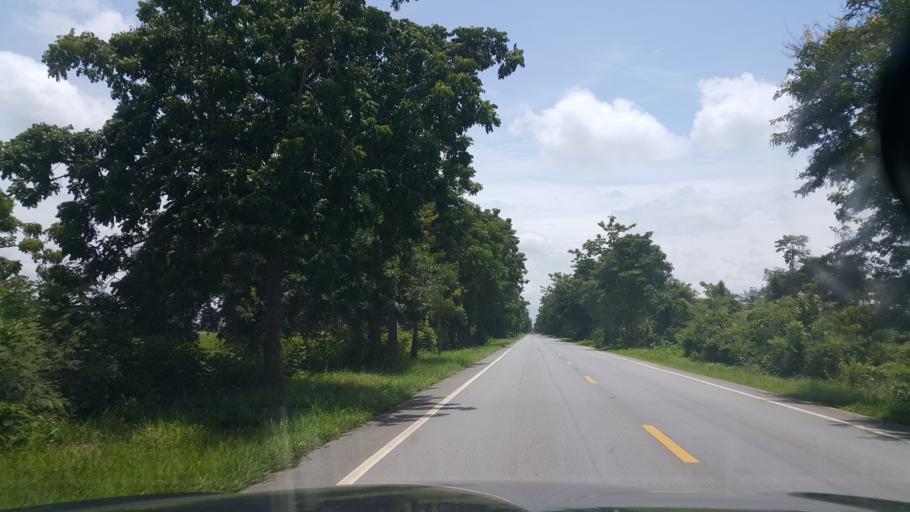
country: TH
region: Sukhothai
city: Sawankhalok
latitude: 17.3269
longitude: 99.7384
